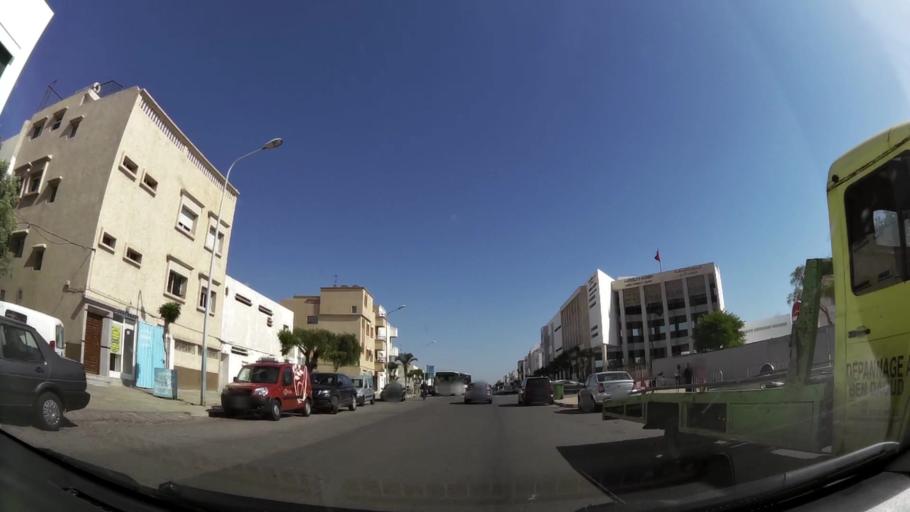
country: MA
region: Souss-Massa-Draa
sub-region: Agadir-Ida-ou-Tnan
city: Agadir
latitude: 30.4180
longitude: -9.5905
